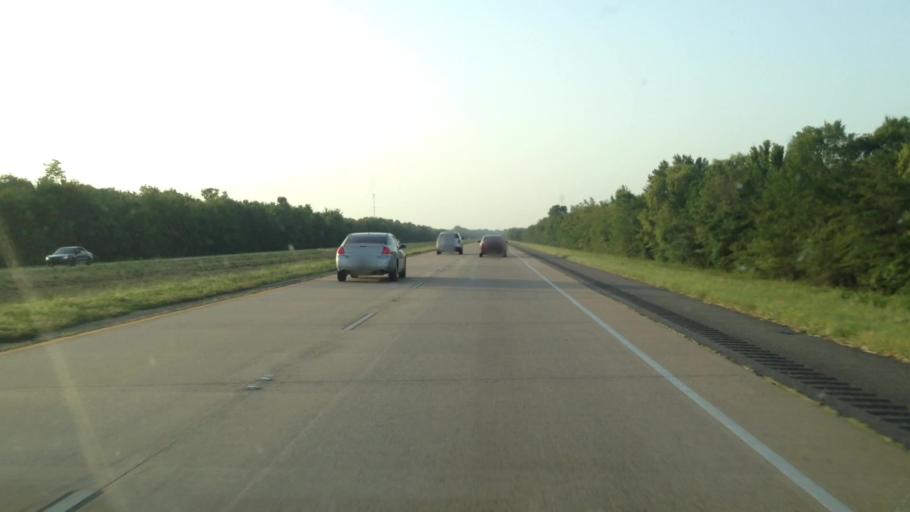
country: US
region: Louisiana
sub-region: Natchitoches Parish
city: Vienna Bend
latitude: 31.5626
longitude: -92.9849
